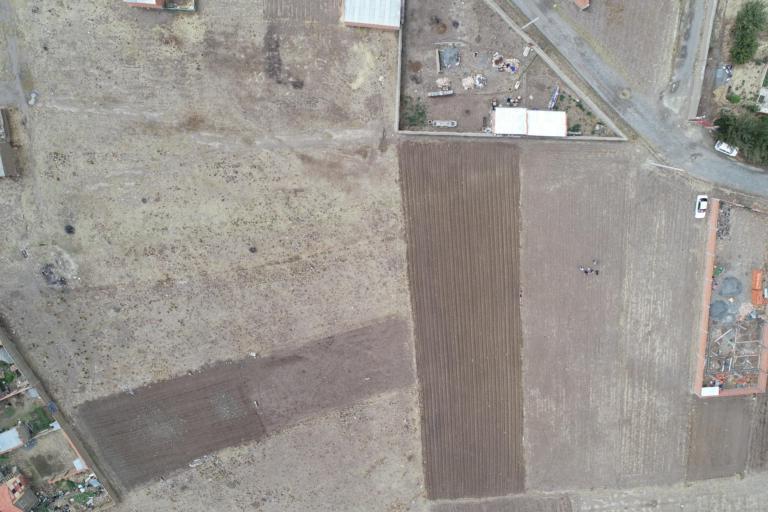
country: BO
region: La Paz
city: Achacachi
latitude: -16.0339
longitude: -68.6906
